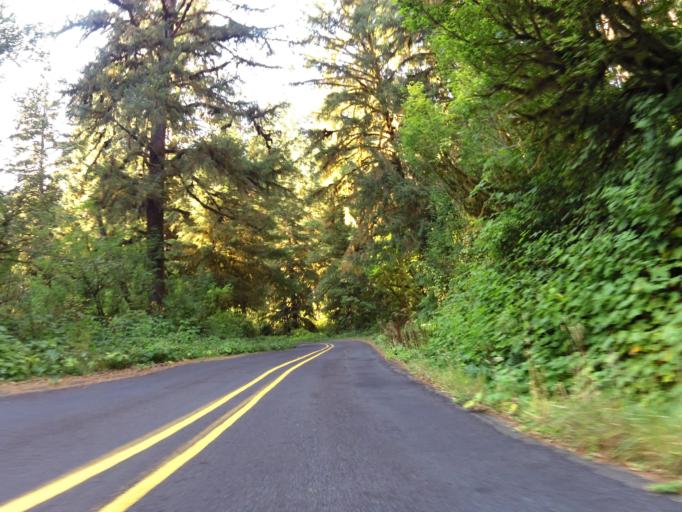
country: US
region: Oregon
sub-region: Lincoln County
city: Rose Lodge
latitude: 45.0368
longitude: -123.9132
